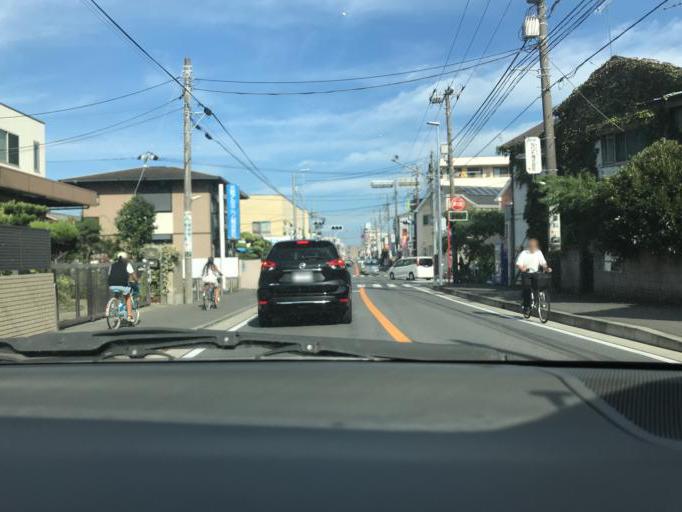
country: JP
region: Kanagawa
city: Fujisawa
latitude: 35.3419
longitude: 139.4560
